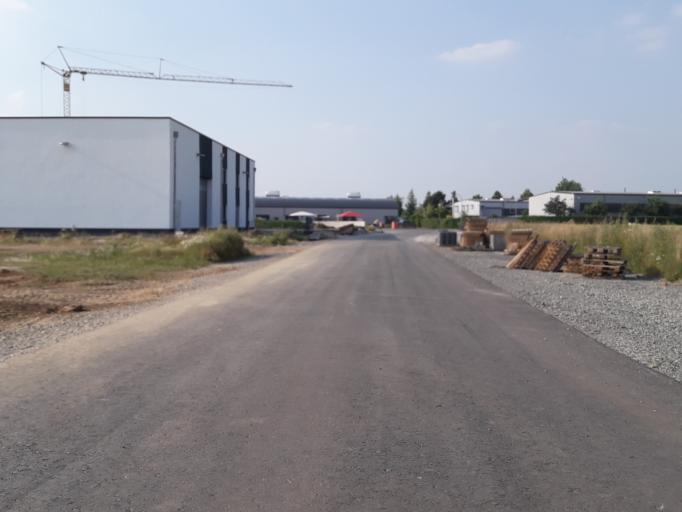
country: DE
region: North Rhine-Westphalia
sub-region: Regierungsbezirk Detmold
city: Salzkotten
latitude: 51.6702
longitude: 8.5793
